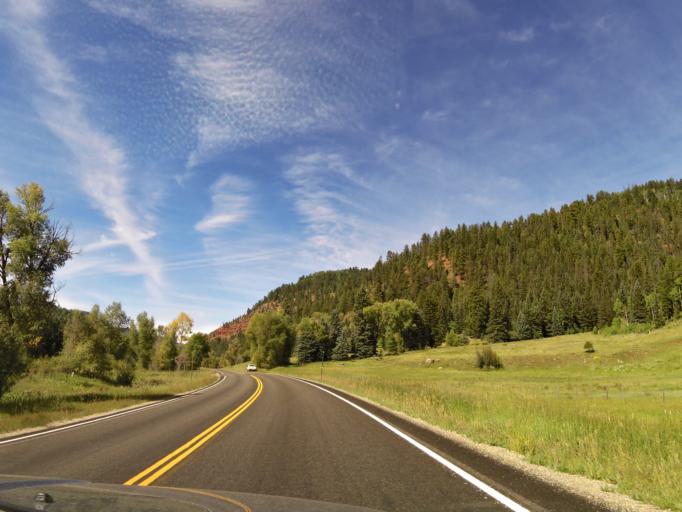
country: US
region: Colorado
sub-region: Montezuma County
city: Mancos
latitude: 37.5937
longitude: -108.1339
